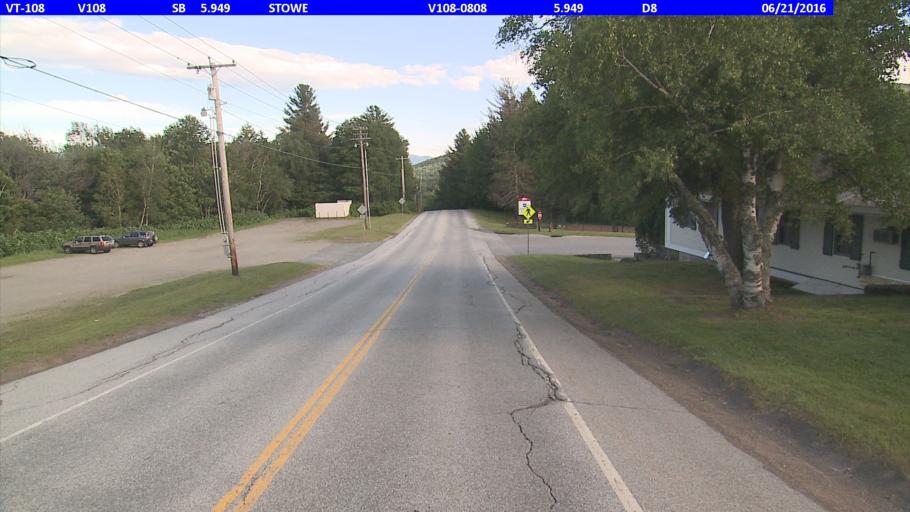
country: US
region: Vermont
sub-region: Lamoille County
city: Morristown
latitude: 44.5113
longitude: -72.7653
